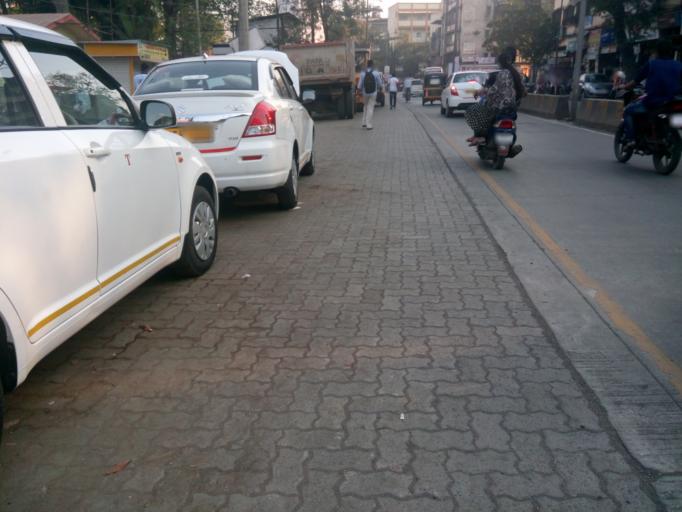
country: IN
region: Maharashtra
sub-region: Thane
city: Dombivli
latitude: 19.2116
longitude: 73.0928
